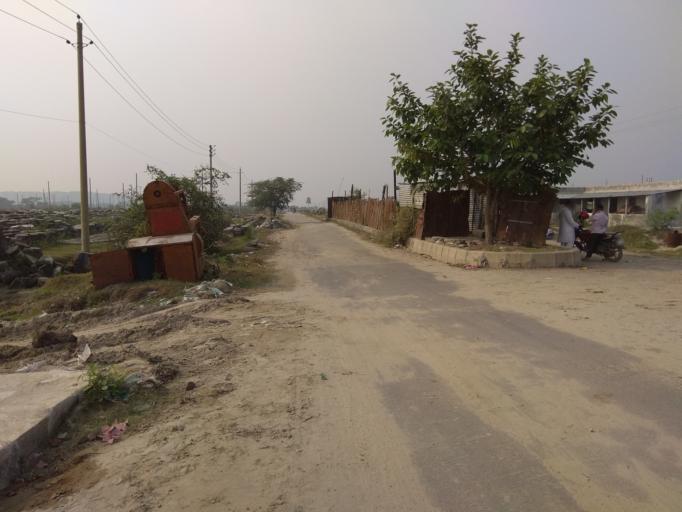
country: BD
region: Dhaka
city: Tungi
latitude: 23.8601
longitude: 90.3709
